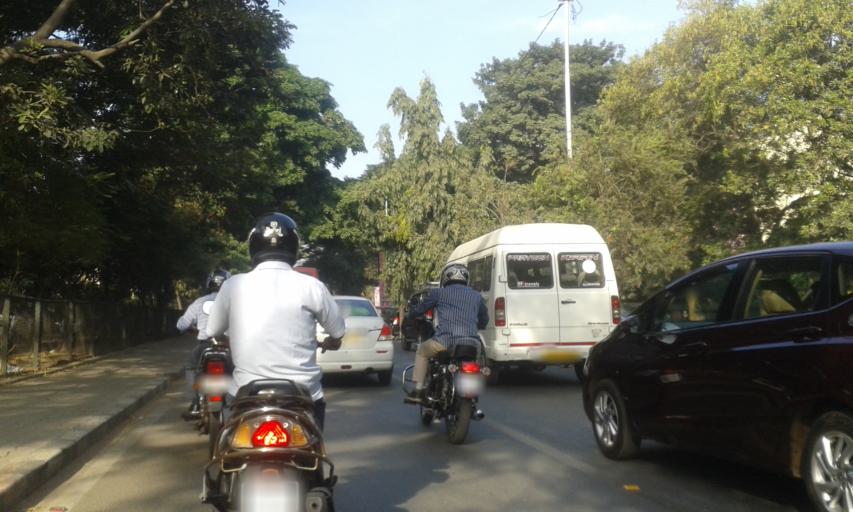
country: IN
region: Karnataka
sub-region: Bangalore Urban
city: Bangalore
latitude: 12.9608
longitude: 77.6398
